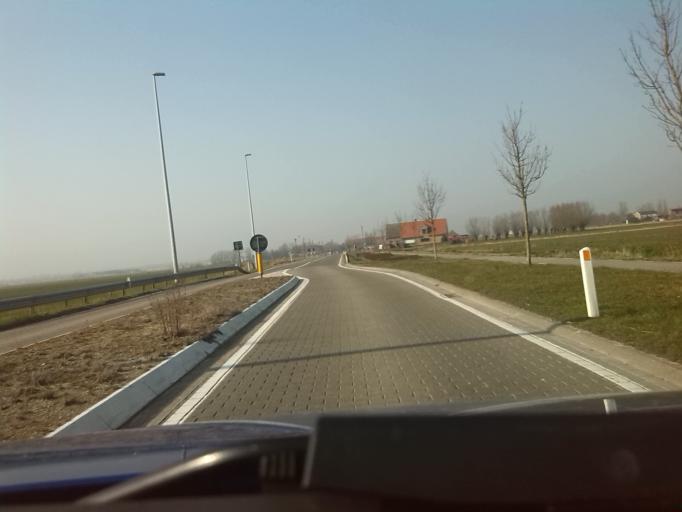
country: BE
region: Flanders
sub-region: Provincie West-Vlaanderen
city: Wenduine
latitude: 51.2695
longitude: 3.0943
